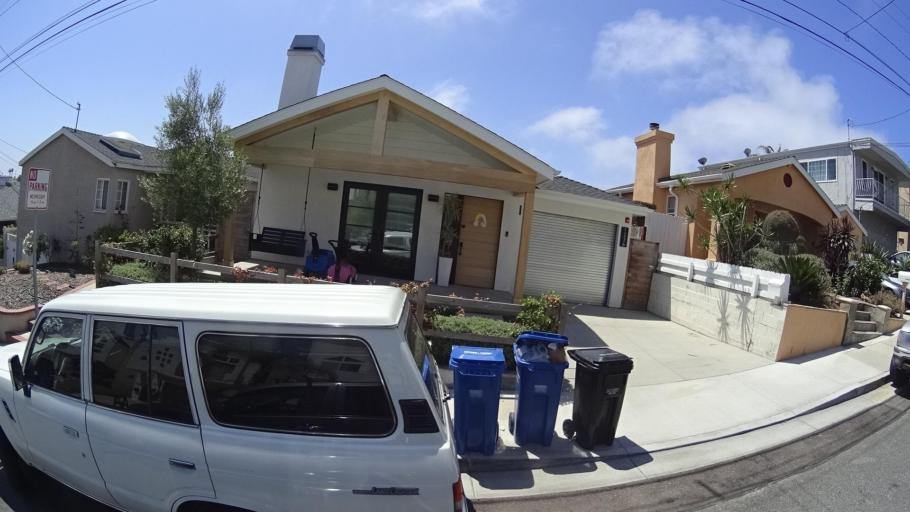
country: US
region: California
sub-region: Los Angeles County
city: Redondo Beach
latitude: 33.8620
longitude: -118.3862
